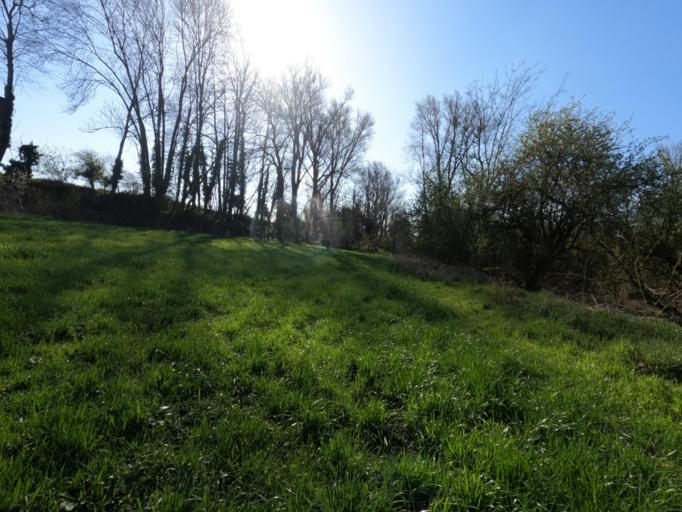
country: DE
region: North Rhine-Westphalia
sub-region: Regierungsbezirk Koln
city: Linnich
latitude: 50.9887
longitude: 6.2880
